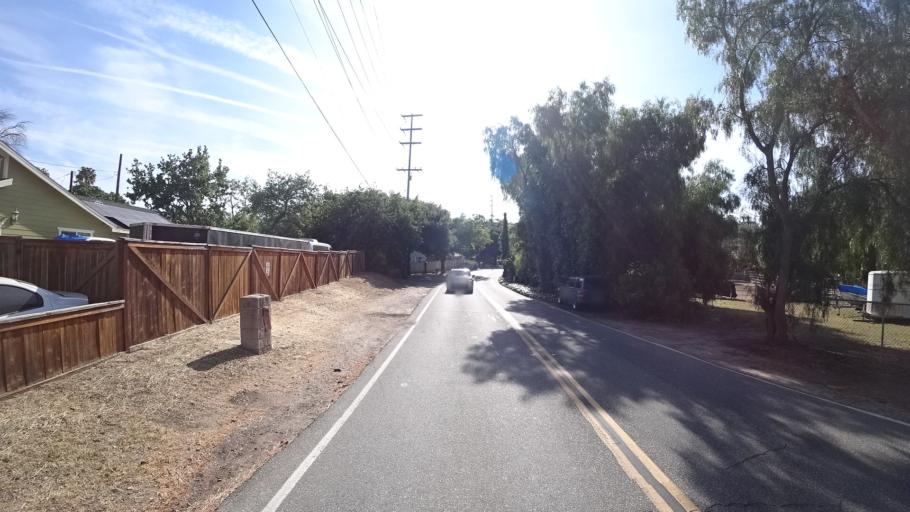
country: US
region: California
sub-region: Ventura County
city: Thousand Oaks
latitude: 34.1857
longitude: -118.8682
